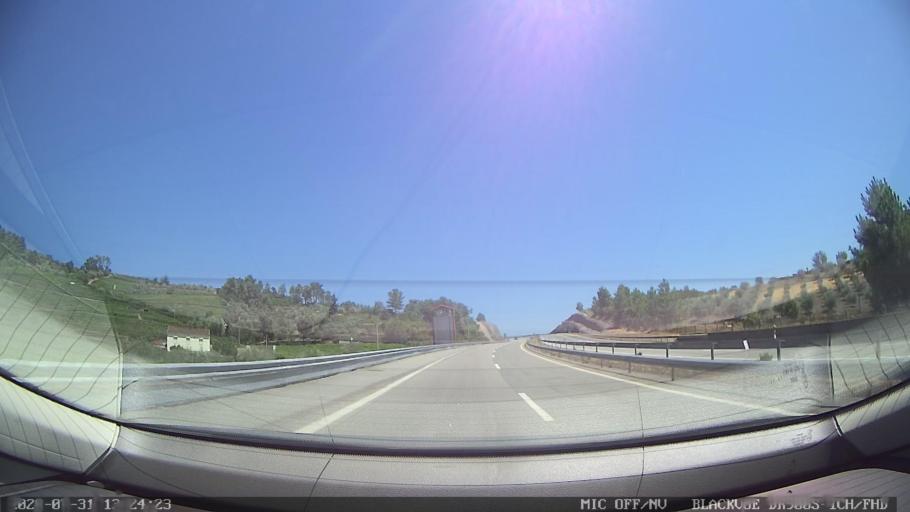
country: PT
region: Vila Real
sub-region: Santa Marta de Penaguiao
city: Santa Marta de Penaguiao
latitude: 41.2083
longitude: -7.7417
